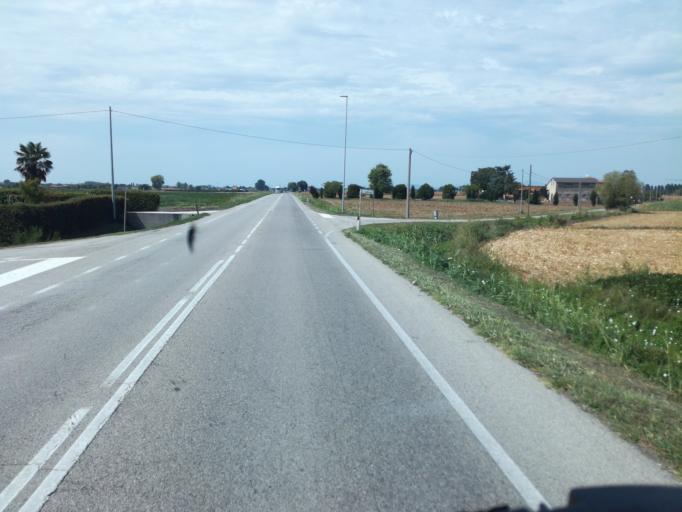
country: IT
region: Veneto
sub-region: Provincia di Padova
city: Candiana
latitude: 45.2136
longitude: 12.0092
